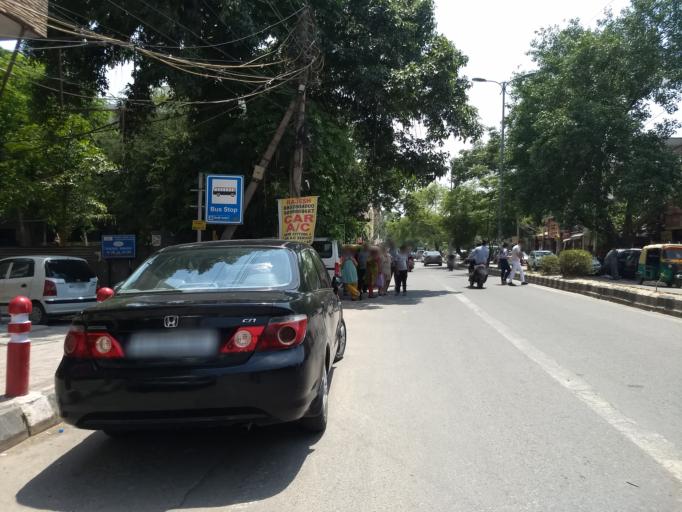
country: IN
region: NCT
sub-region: New Delhi
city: New Delhi
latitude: 28.5368
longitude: 77.2100
